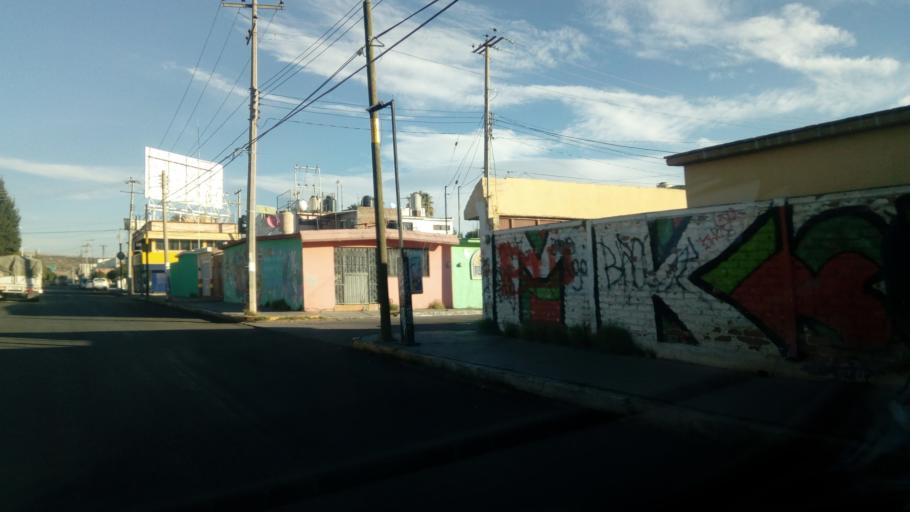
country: MX
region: Durango
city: Victoria de Durango
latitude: 24.0653
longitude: -104.5989
